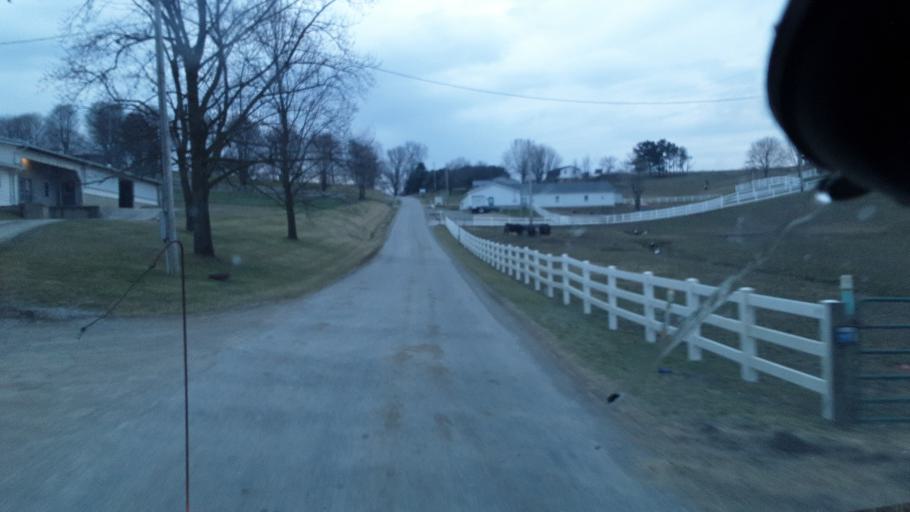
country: US
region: Ohio
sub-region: Tuscarawas County
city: Sugarcreek
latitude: 40.5007
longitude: -81.6796
